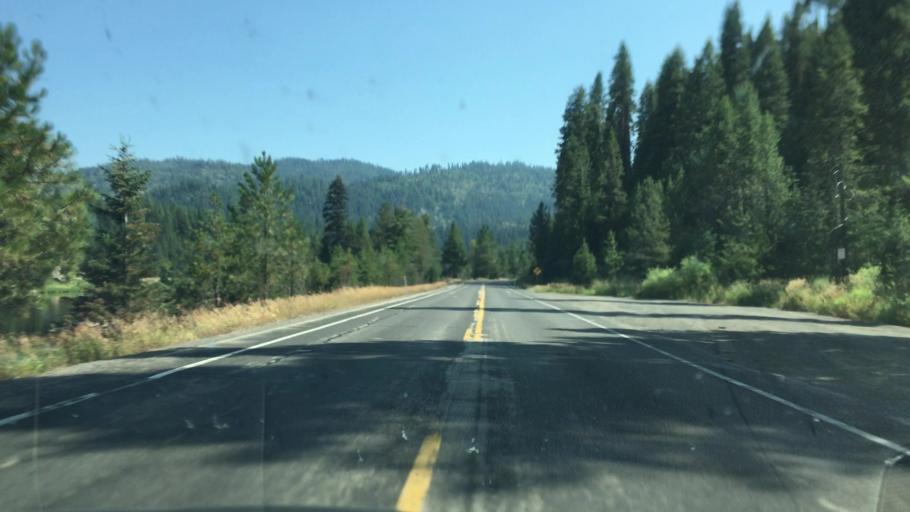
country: US
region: Idaho
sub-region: Valley County
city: Cascade
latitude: 44.2800
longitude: -116.0790
